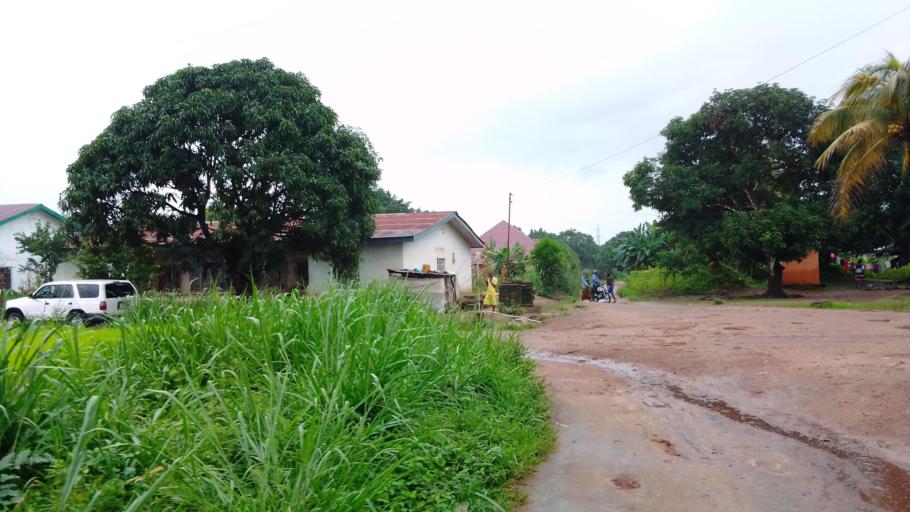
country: SL
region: Eastern Province
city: Kenema
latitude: 7.8986
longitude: -11.1800
